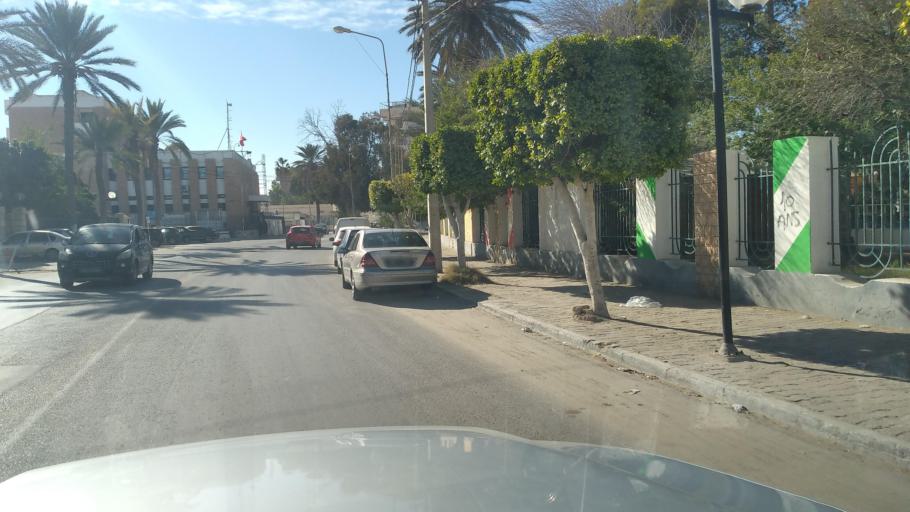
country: TN
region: Qabis
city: Gabes
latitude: 33.8878
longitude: 10.1100
